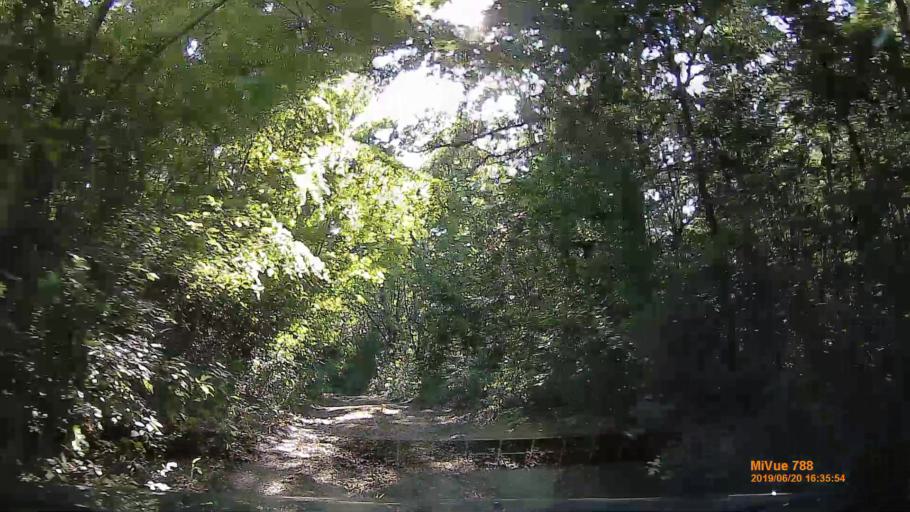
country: HU
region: Baranya
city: Buekkoesd
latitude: 46.1720
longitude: 18.0393
